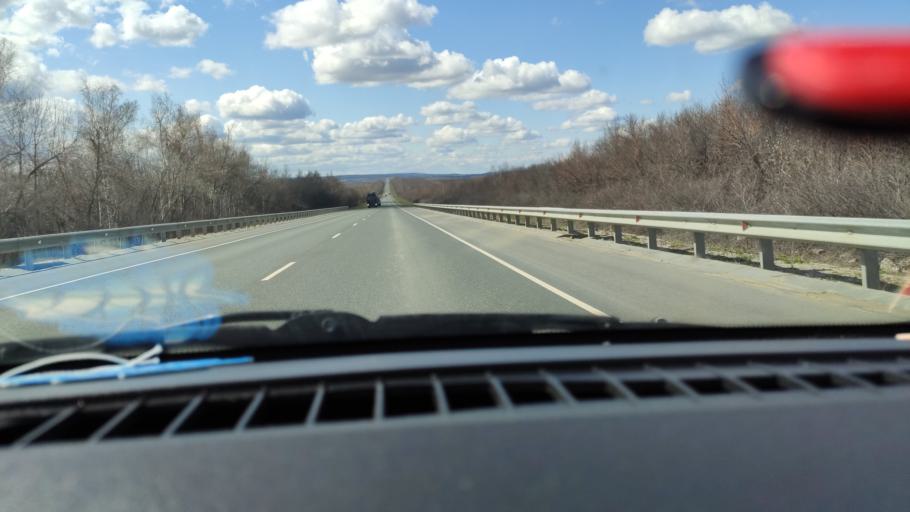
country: RU
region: Saratov
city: Khvalynsk
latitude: 52.6130
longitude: 48.1620
